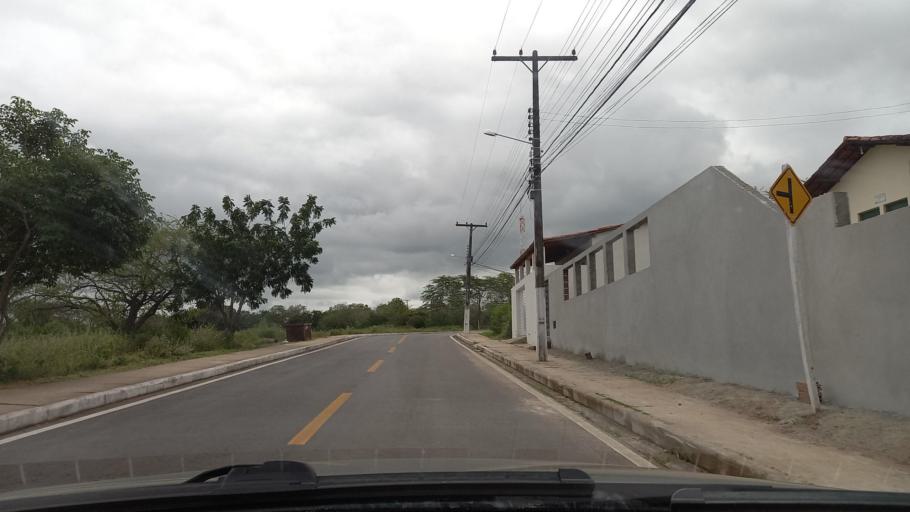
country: BR
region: Sergipe
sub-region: Caninde De Sao Francisco
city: Caninde de Sao Francisco
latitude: -9.6188
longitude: -37.7662
